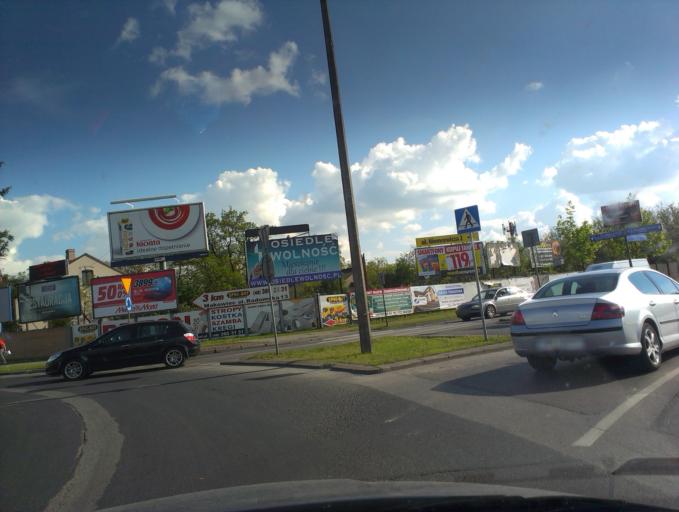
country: PL
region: Masovian Voivodeship
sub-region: Radom
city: Radom
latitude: 51.3821
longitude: 21.1797
